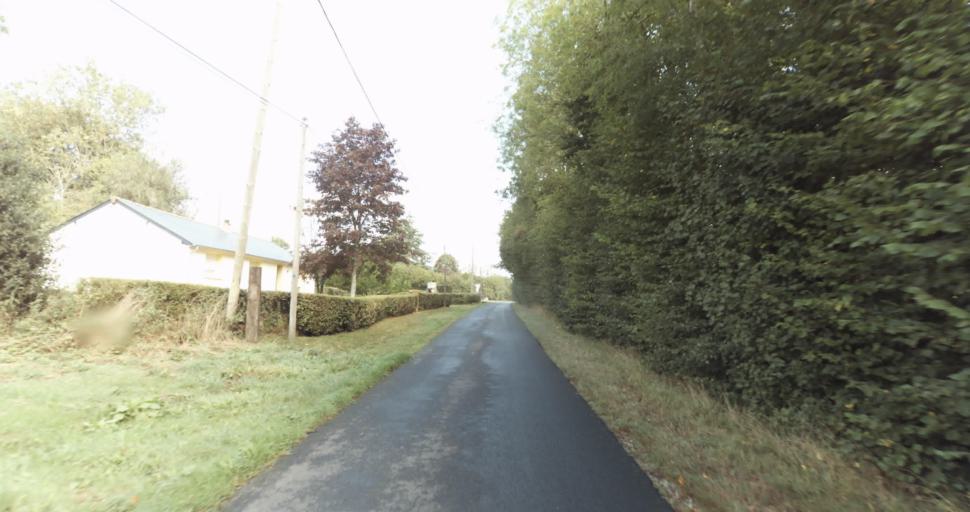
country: FR
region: Lower Normandy
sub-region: Departement du Calvados
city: Orbec
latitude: 48.9532
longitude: 0.3753
